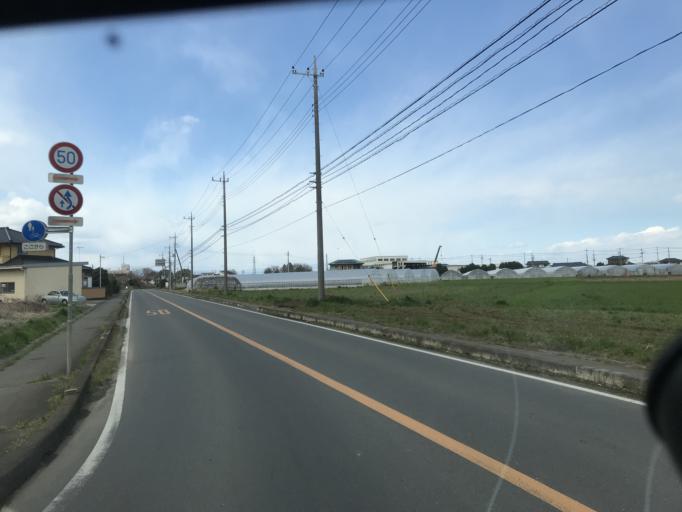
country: JP
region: Ibaraki
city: Shimodate
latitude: 36.2482
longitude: 139.9367
